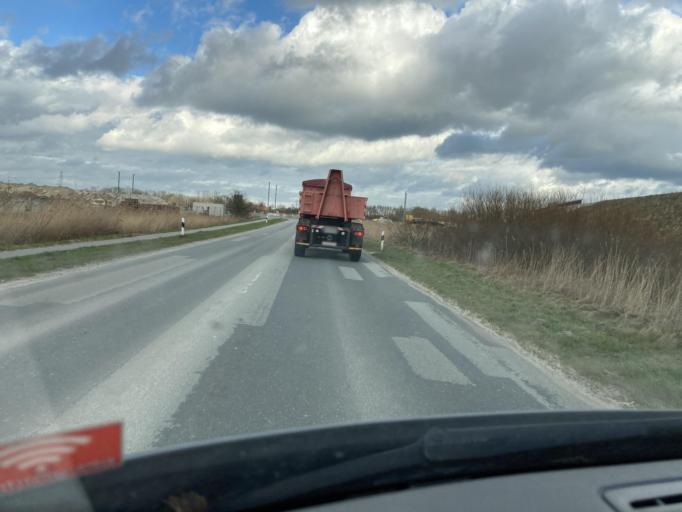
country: DE
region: Lower Saxony
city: Sande
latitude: 53.5156
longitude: 8.0228
